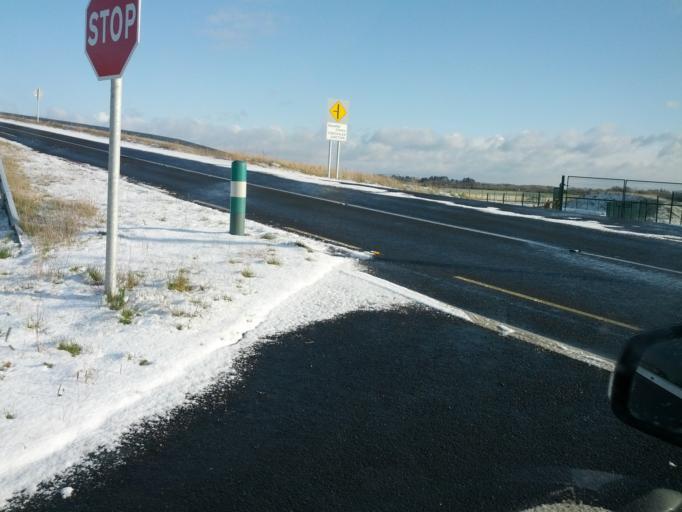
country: IE
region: Connaught
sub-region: County Galway
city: Oranmore
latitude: 53.1972
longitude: -8.8309
